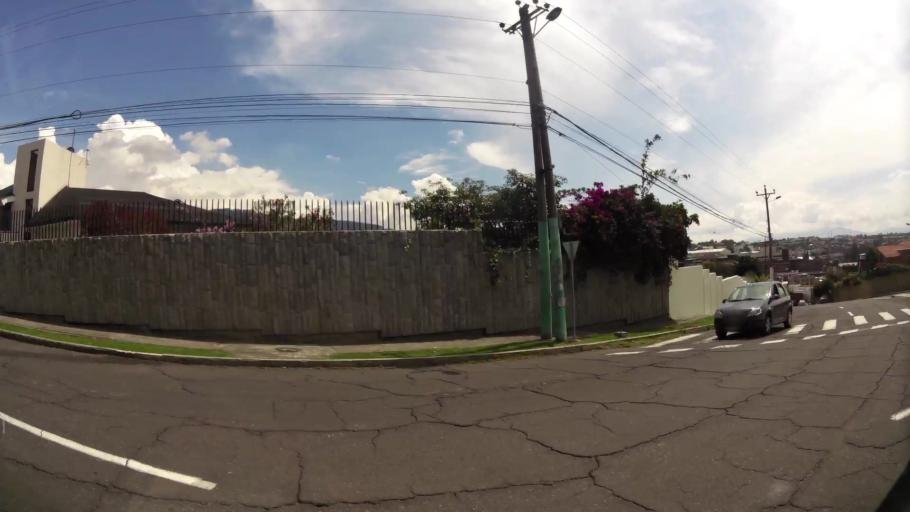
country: EC
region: Pichincha
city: Quito
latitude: -0.2121
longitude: -78.4268
